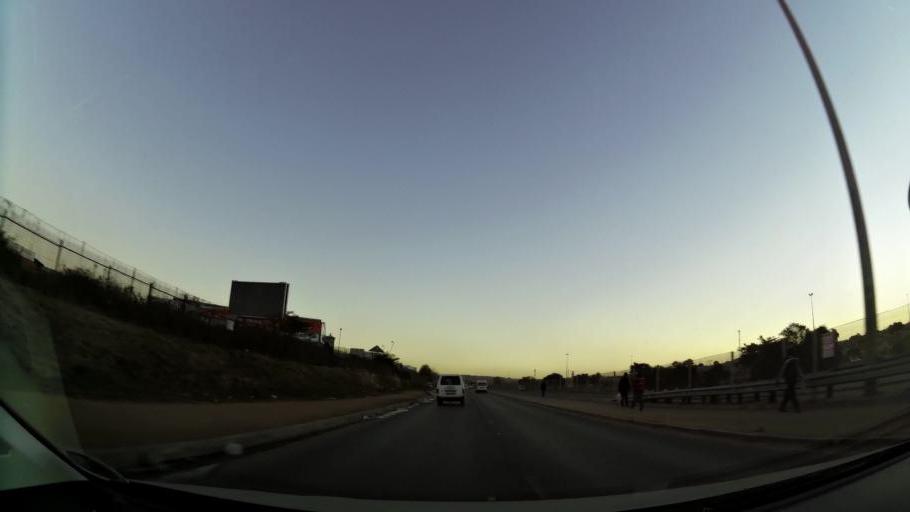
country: ZA
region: Gauteng
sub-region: Ekurhuleni Metropolitan Municipality
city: Tembisa
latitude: -26.0244
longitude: 28.1968
